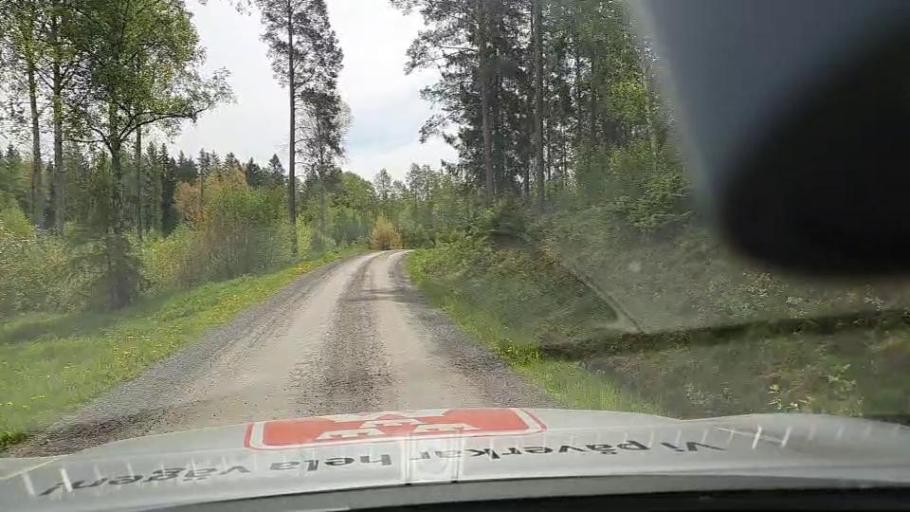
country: SE
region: Soedermanland
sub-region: Eskilstuna Kommun
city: Arla
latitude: 59.2617
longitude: 16.8248
